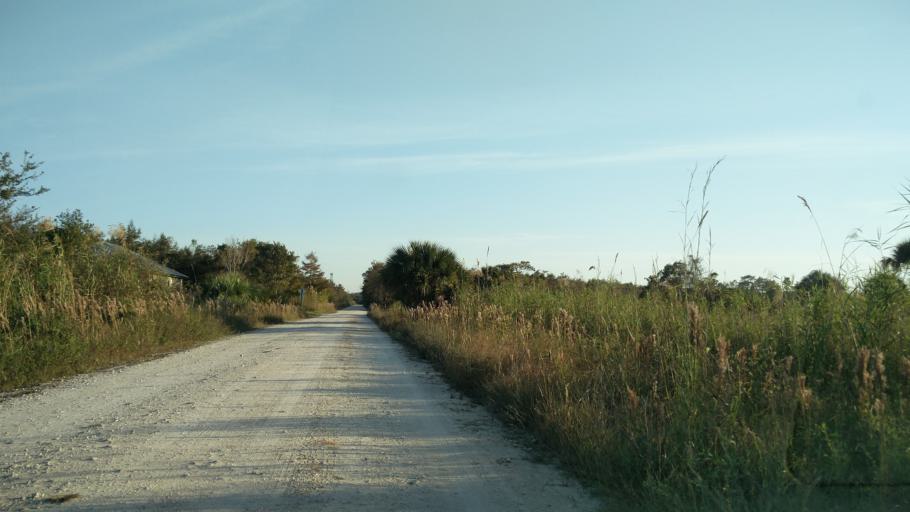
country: US
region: Florida
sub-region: Collier County
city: Lely Resort
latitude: 25.9579
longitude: -81.3631
